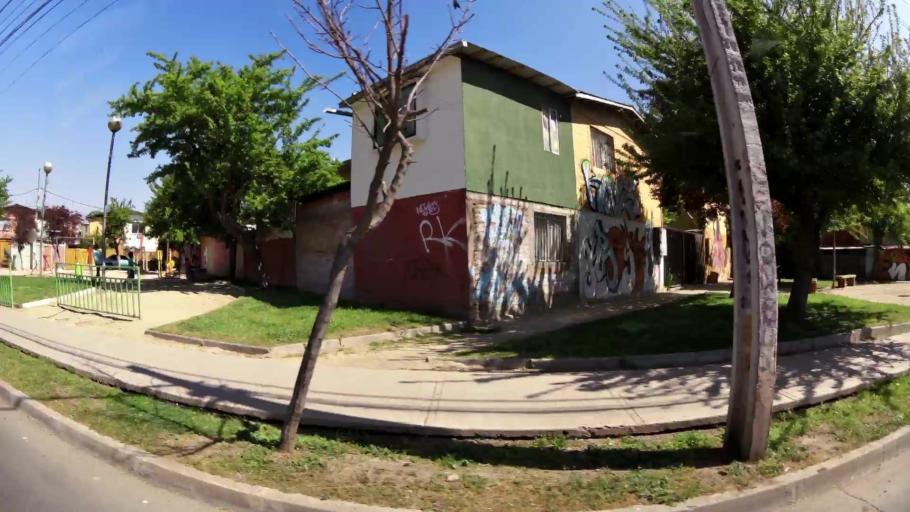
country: CL
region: Santiago Metropolitan
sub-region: Provincia de Santiago
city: Lo Prado
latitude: -33.3532
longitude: -70.7154
